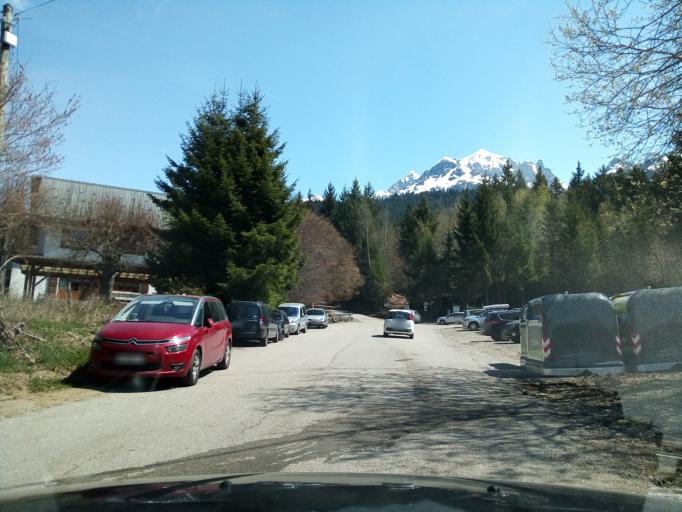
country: FR
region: Rhone-Alpes
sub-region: Departement de l'Isere
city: Revel
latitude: 45.1870
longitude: 5.8987
